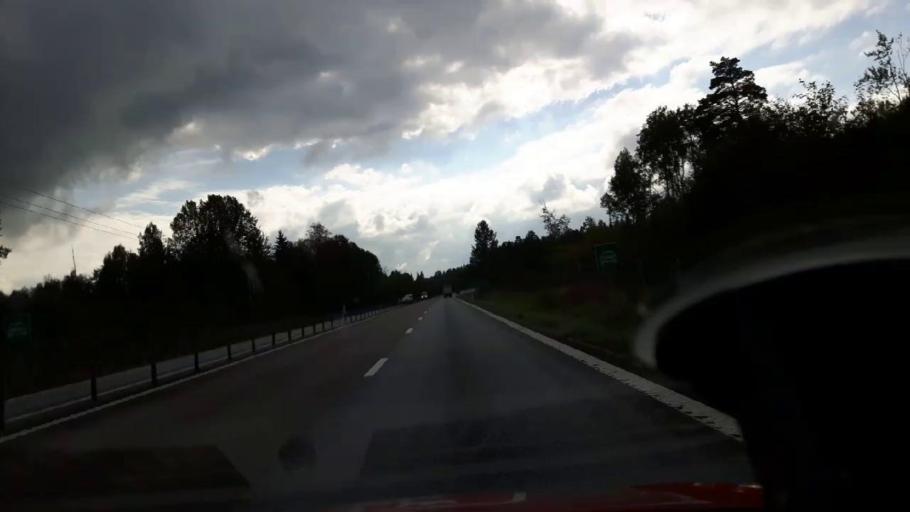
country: SE
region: Gaevleborg
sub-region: Gavle Kommun
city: Norrsundet
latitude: 60.9556
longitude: 17.0340
